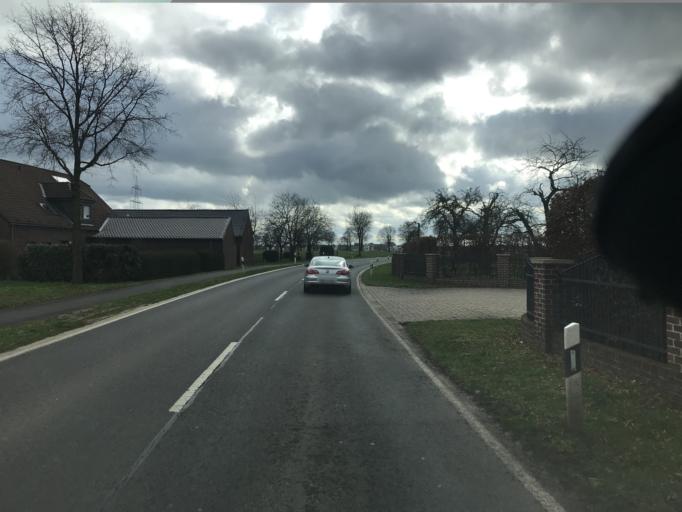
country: DE
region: North Rhine-Westphalia
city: Tonisvorst
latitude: 51.2637
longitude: 6.4623
